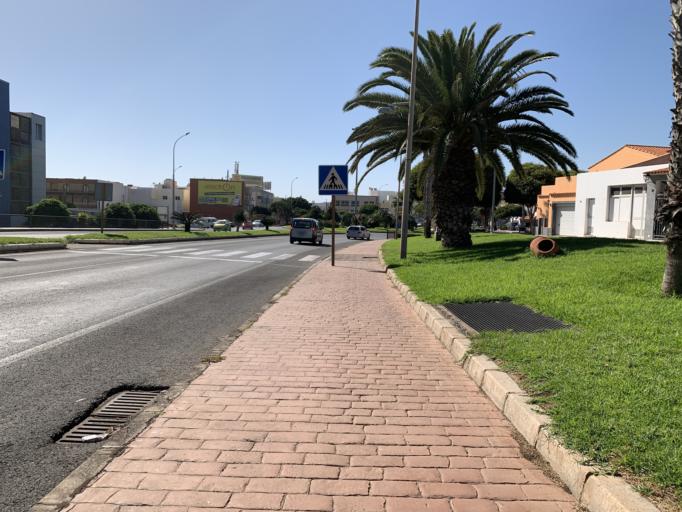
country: ES
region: Canary Islands
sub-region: Provincia de Las Palmas
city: Puerto del Rosario
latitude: 28.4962
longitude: -13.8643
